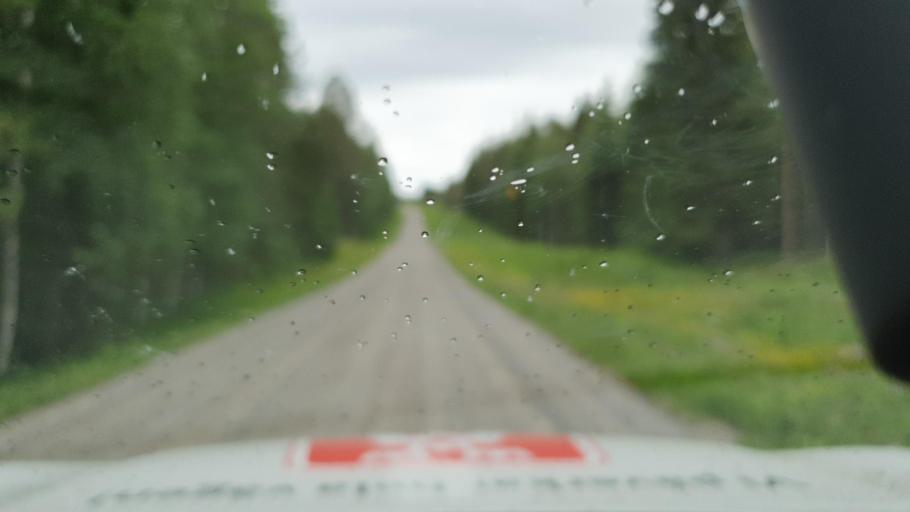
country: SE
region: Vaesterbotten
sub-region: Nordmalings Kommun
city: Nordmaling
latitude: 63.7451
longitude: 19.5010
